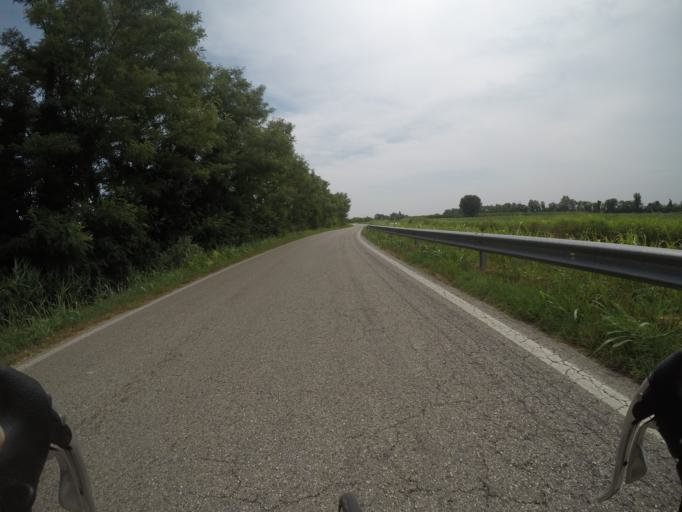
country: IT
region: Veneto
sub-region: Provincia di Rovigo
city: Villanova del Ghebbo Canton
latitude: 45.0532
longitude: 11.6637
